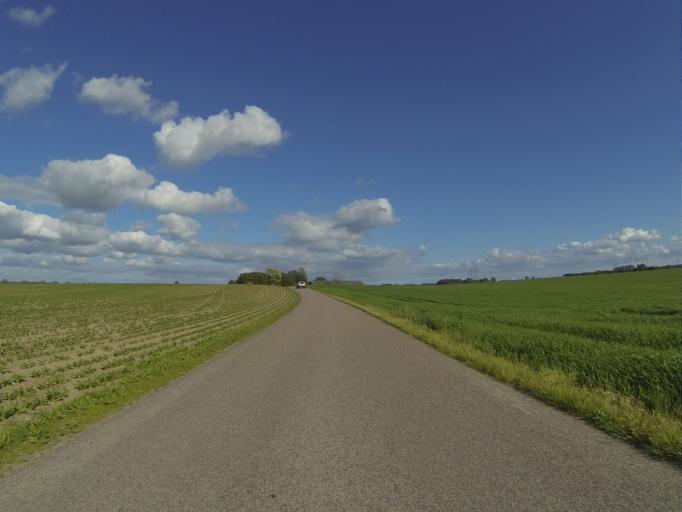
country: SE
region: Skane
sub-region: Staffanstorps Kommun
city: Staffanstorp
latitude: 55.6666
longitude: 13.2111
